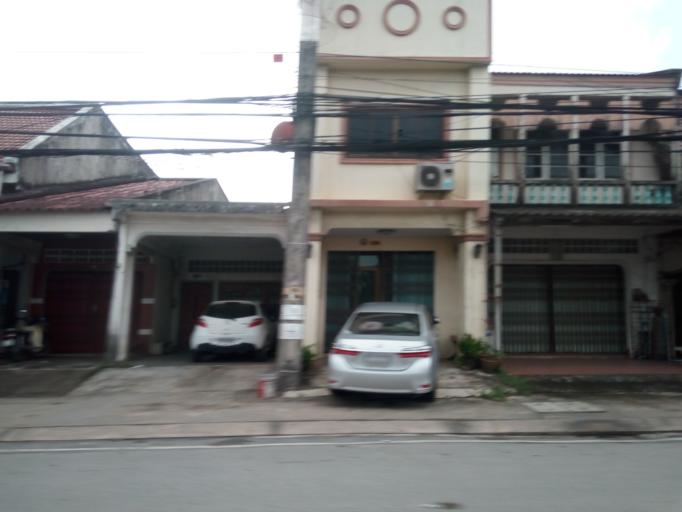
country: TH
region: Phuket
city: Thalang
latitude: 8.0288
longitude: 98.3331
